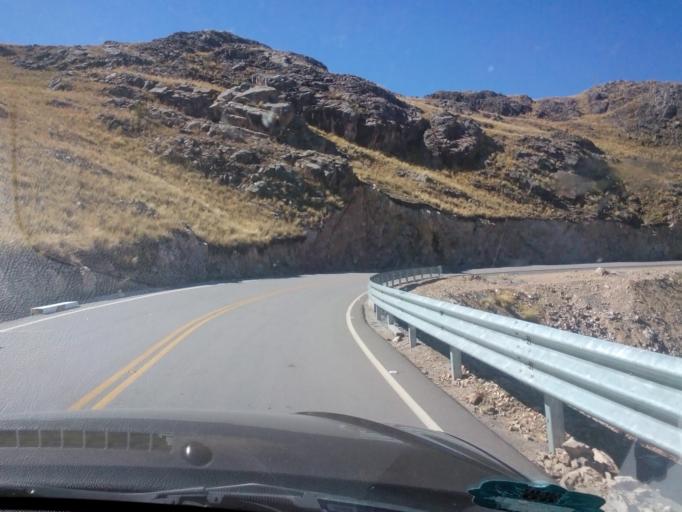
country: PE
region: Ayacucho
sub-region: Provincia de Huamanga
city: Acocro
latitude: -13.3655
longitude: -74.0812
